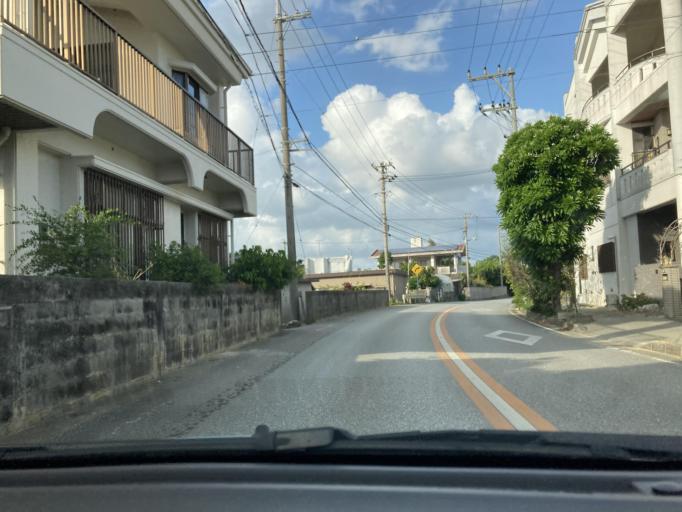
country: JP
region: Okinawa
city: Itoman
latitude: 26.1077
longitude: 127.6653
